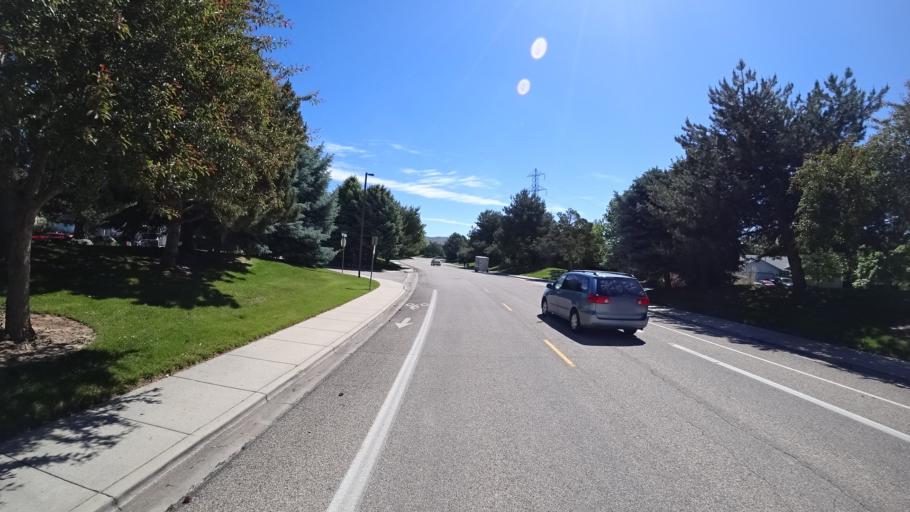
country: US
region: Idaho
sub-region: Ada County
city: Boise
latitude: 43.5515
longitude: -116.1315
